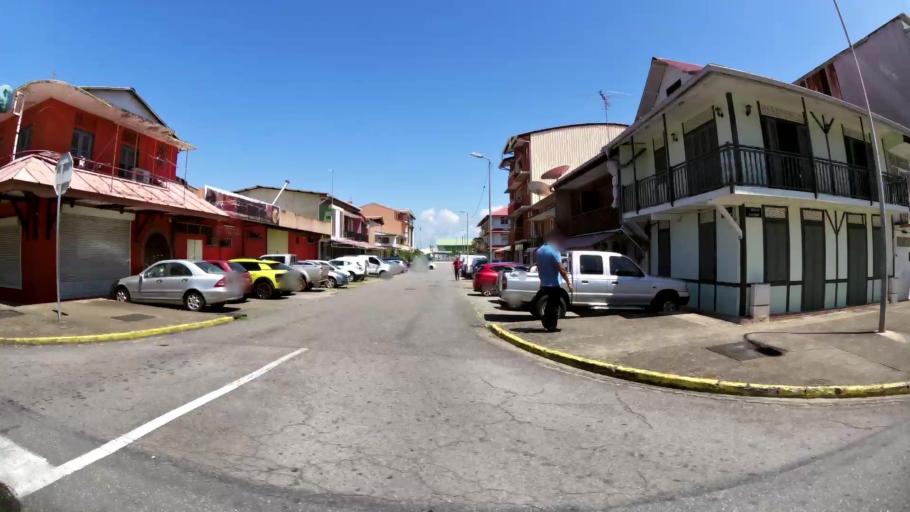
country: GF
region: Guyane
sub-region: Guyane
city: Cayenne
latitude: 4.9419
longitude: -52.3240
